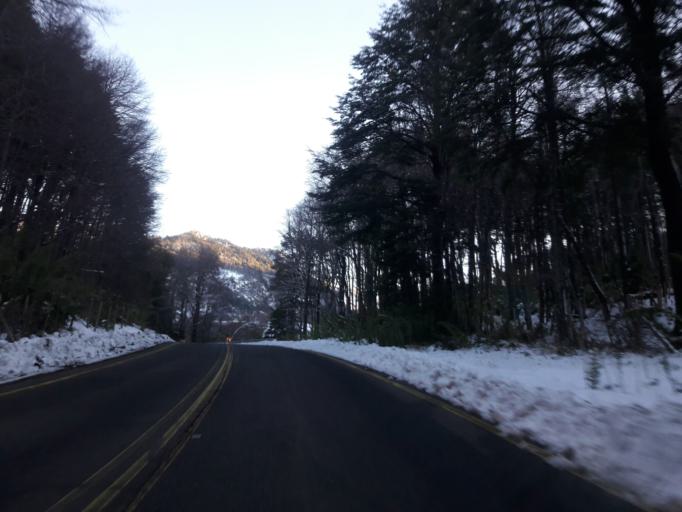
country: CL
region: Araucania
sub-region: Provincia de Cautin
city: Vilcun
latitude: -38.5044
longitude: -71.5208
